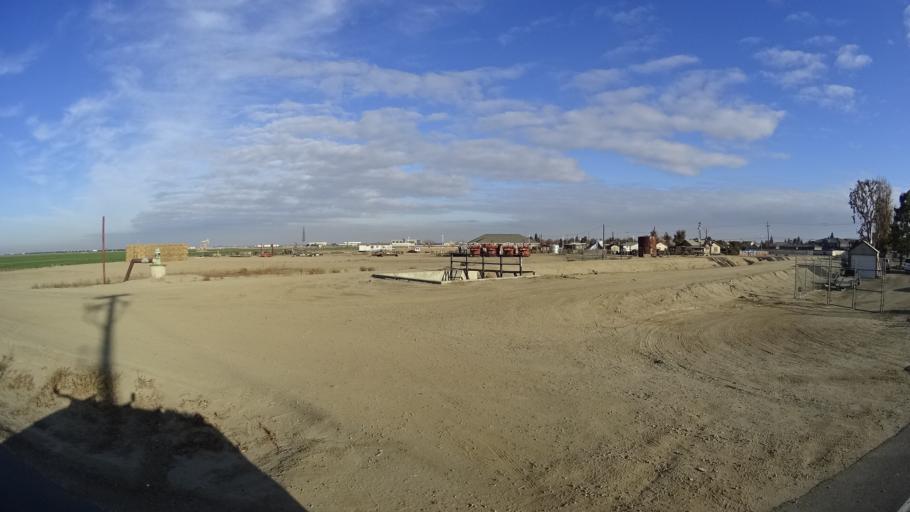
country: US
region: California
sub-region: Kern County
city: Rosedale
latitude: 35.3034
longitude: -119.1294
